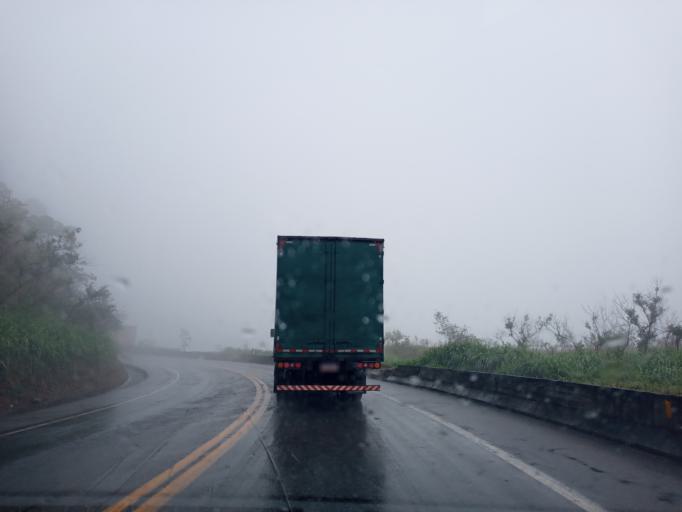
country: BR
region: Minas Gerais
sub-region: Luz
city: Luz
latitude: -19.7082
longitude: -45.9167
